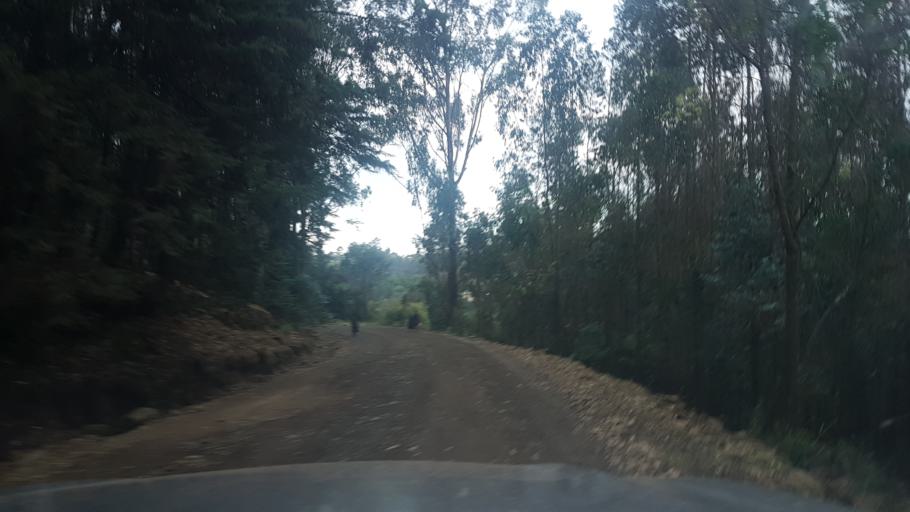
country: ET
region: Amhara
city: Finote Selam
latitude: 10.7881
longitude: 37.6647
